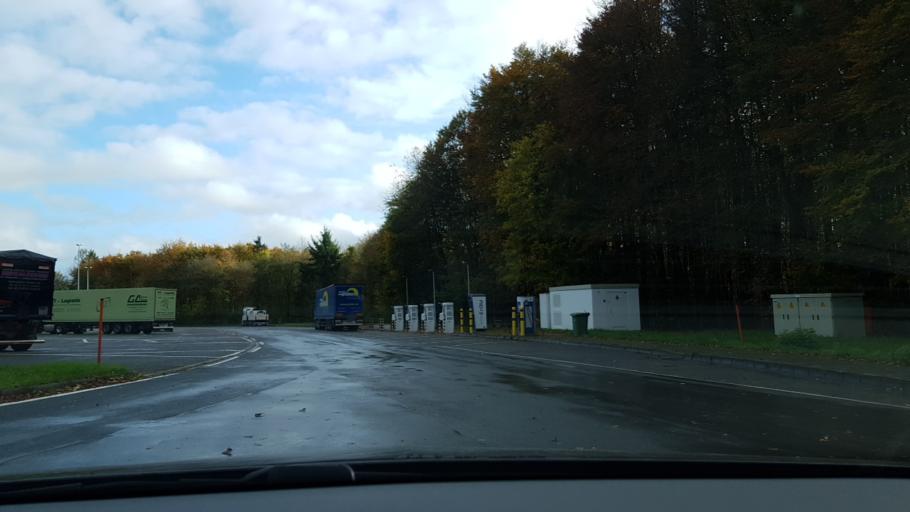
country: DE
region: Rheinland-Pfalz
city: Niederofflingen
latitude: 50.0688
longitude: 6.8798
